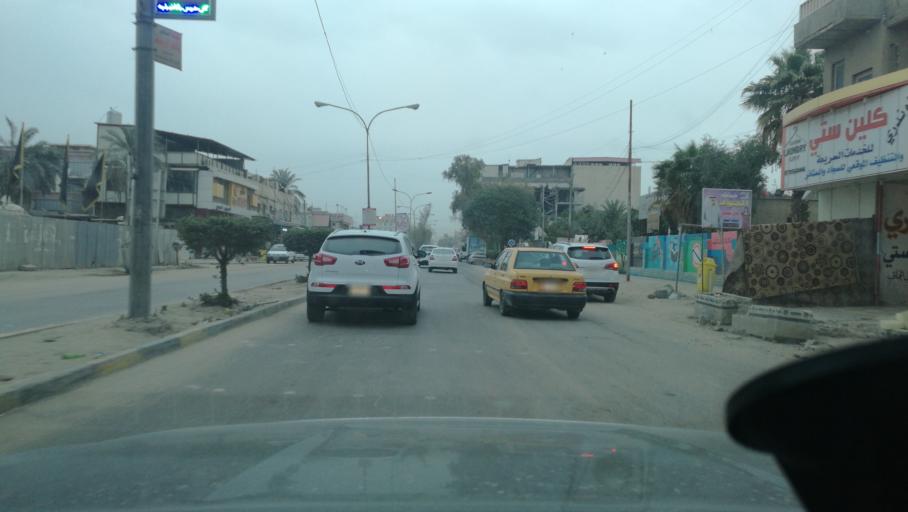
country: IQ
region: Basra Governorate
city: Al Basrah al Qadimah
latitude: 30.5079
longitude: 47.8371
